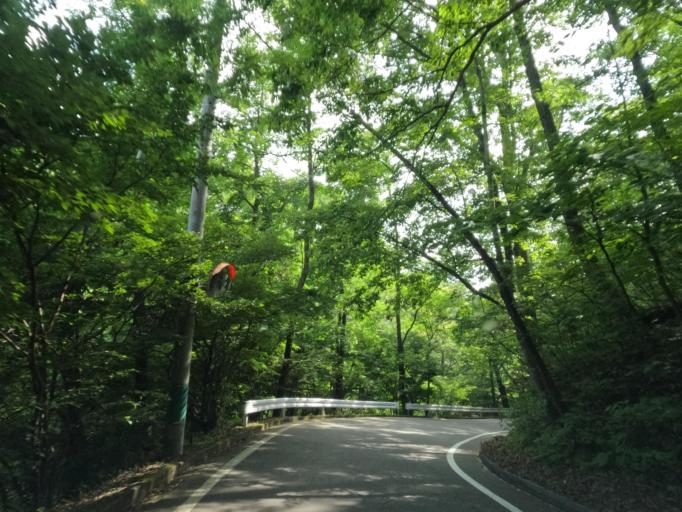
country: JP
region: Nagano
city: Komoro
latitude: 36.3575
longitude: 138.6070
